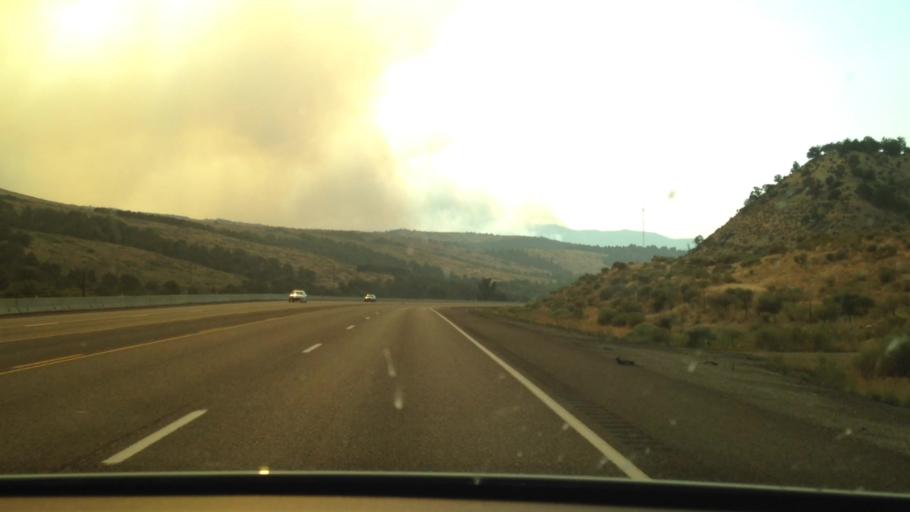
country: US
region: Utah
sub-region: Utah County
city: Mapleton
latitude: 39.9504
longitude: -111.2880
